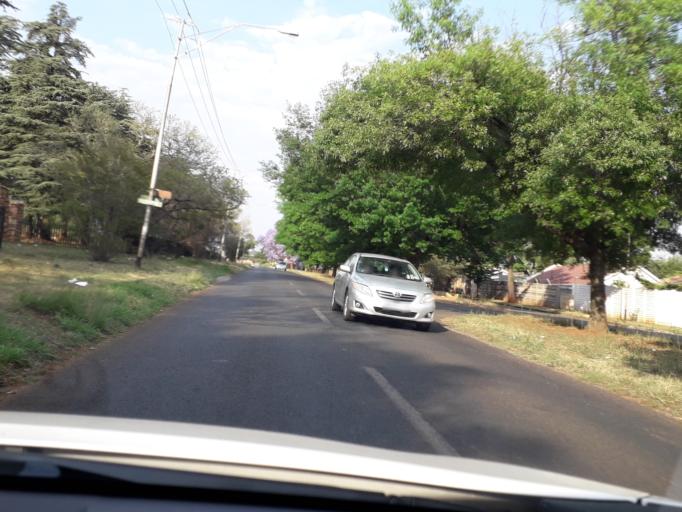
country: ZA
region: Gauteng
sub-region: City of Johannesburg Metropolitan Municipality
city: Johannesburg
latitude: -26.1620
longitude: 27.9848
